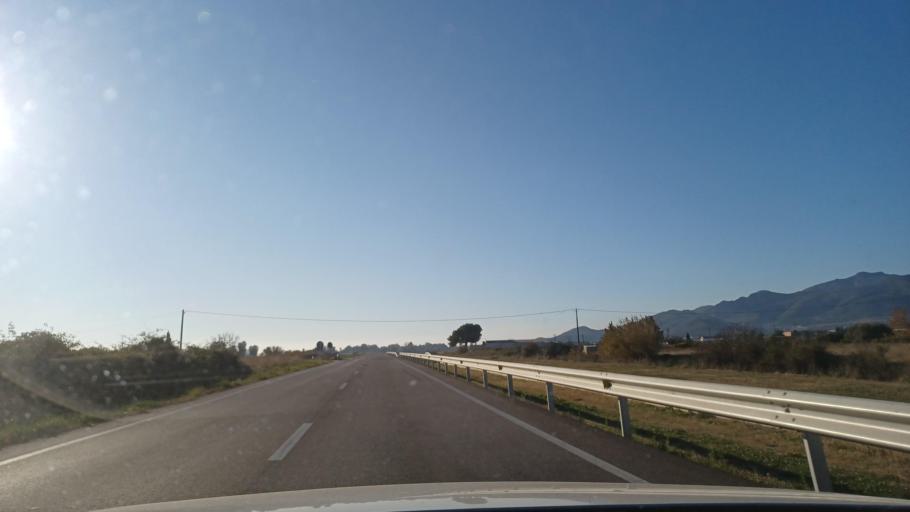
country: ES
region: Catalonia
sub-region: Provincia de Tarragona
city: Amposta
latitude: 40.6945
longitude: 0.5897
